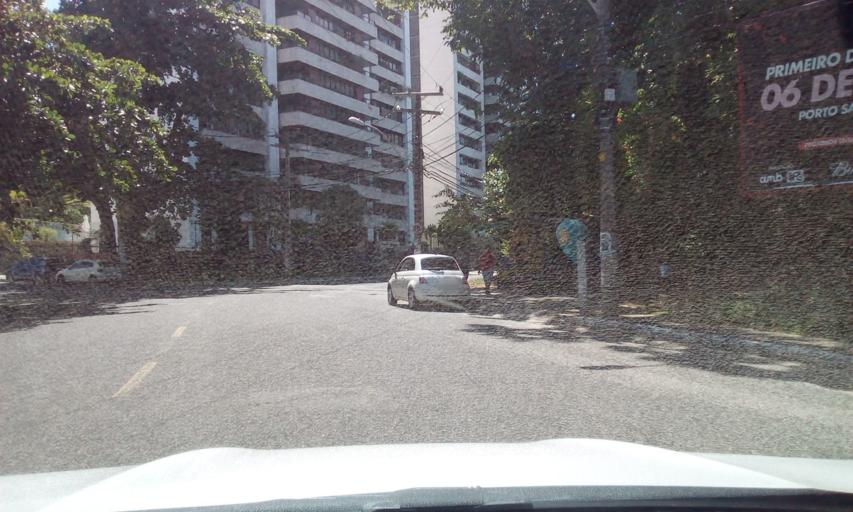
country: BR
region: Bahia
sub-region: Salvador
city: Salvador
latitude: -12.9928
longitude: -38.4649
